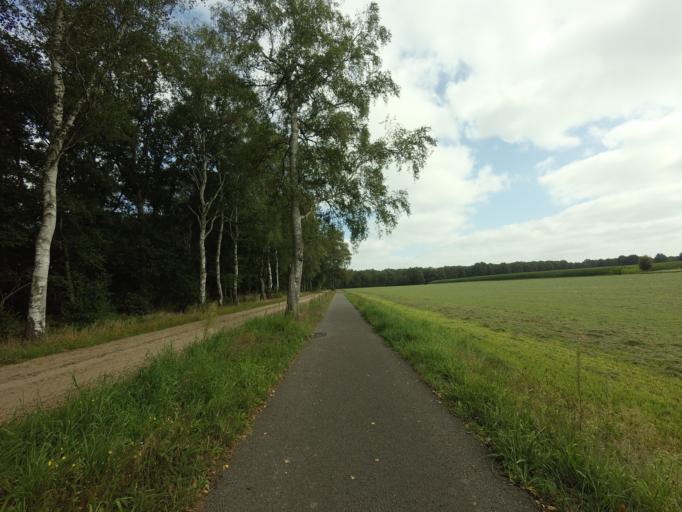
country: NL
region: Drenthe
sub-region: Gemeente Westerveld
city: Havelte
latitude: 52.8489
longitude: 6.2427
